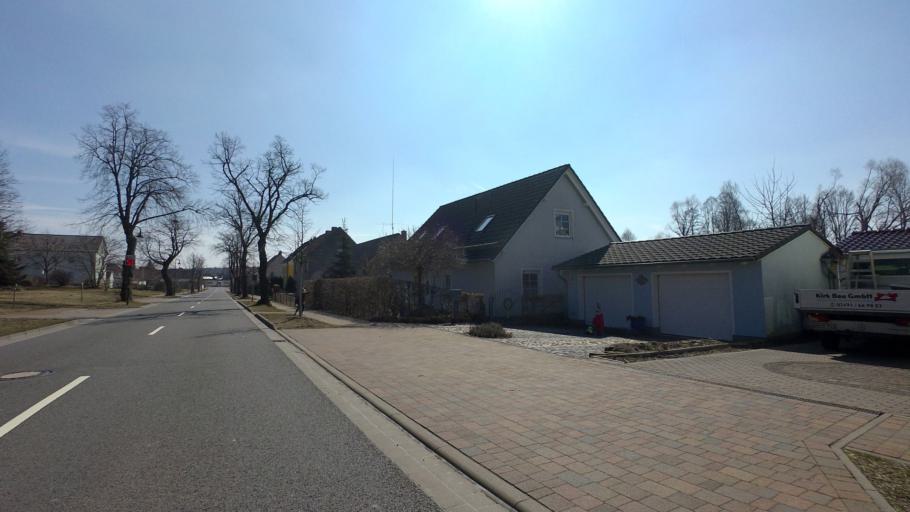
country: DE
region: Saxony-Anhalt
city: Nudersdorf
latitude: 51.9569
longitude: 12.5920
